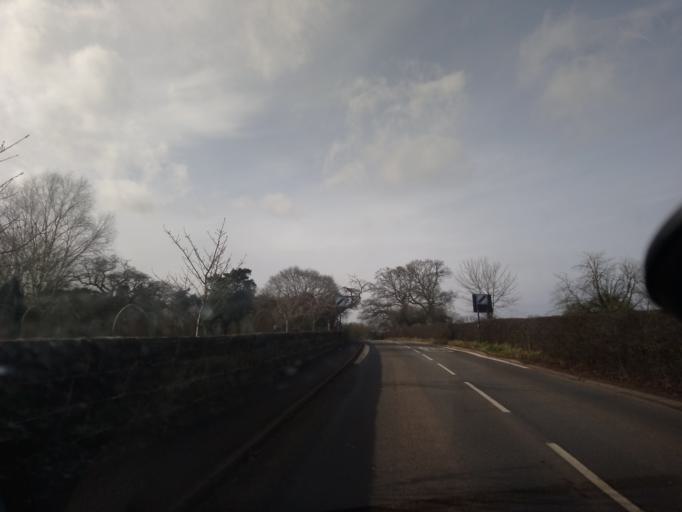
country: GB
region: England
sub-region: Shropshire
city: Stoke upon Tern
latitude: 52.8541
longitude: -2.5769
